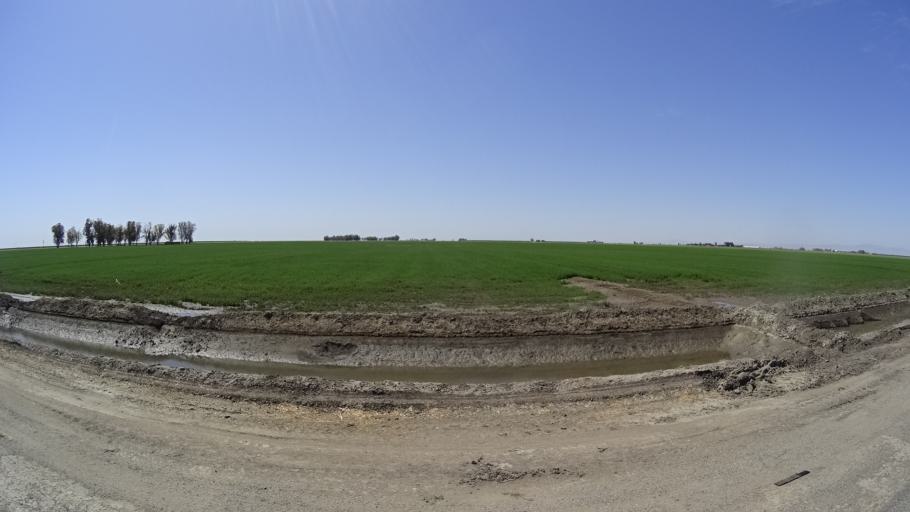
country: US
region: California
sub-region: Kings County
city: Stratford
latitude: 36.1893
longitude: -119.7681
